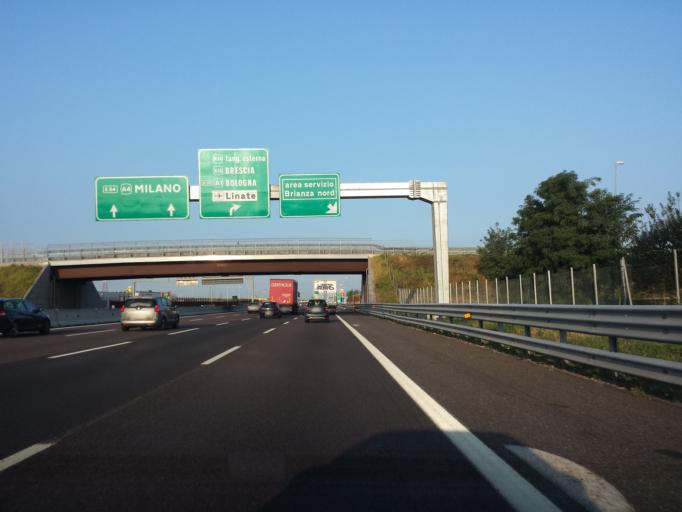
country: IT
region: Lombardy
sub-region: Citta metropolitana di Milano
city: Torrazza dei Mandelli
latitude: 45.5763
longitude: 9.4006
